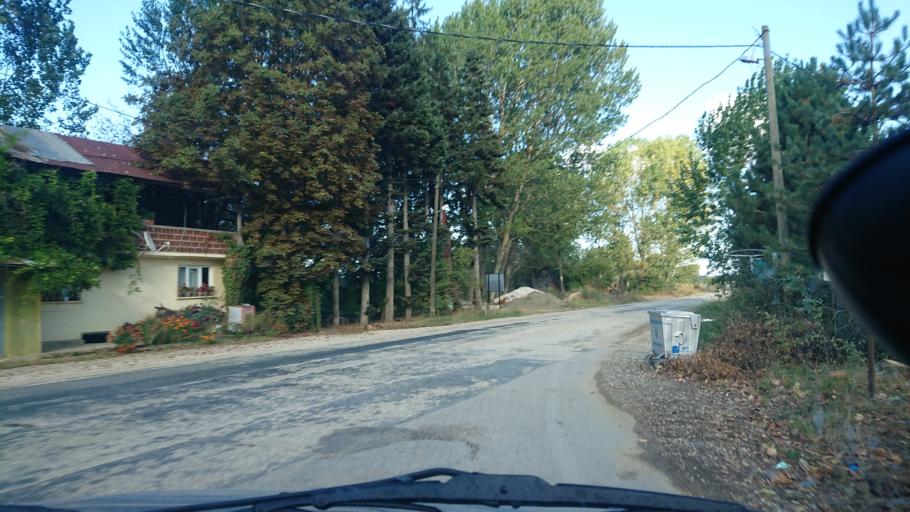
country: TR
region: Bilecik
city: Pazaryeri
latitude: 40.0164
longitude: 29.8365
